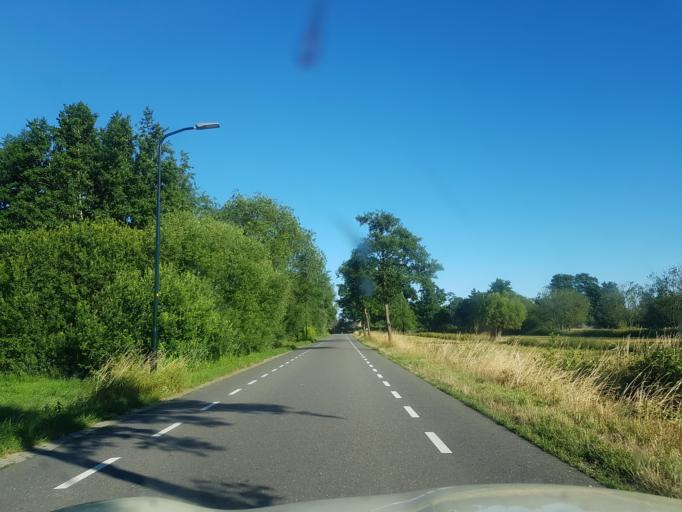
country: NL
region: Gelderland
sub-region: Gemeente Apeldoorn
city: Beekbergen
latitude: 52.1770
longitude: 6.0175
